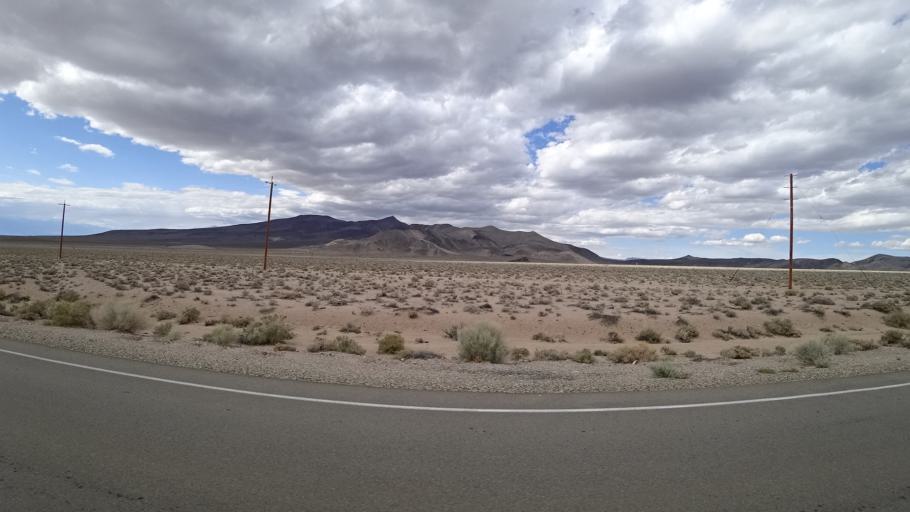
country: US
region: California
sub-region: Inyo County
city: Lone Pine
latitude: 36.3312
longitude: -117.7188
